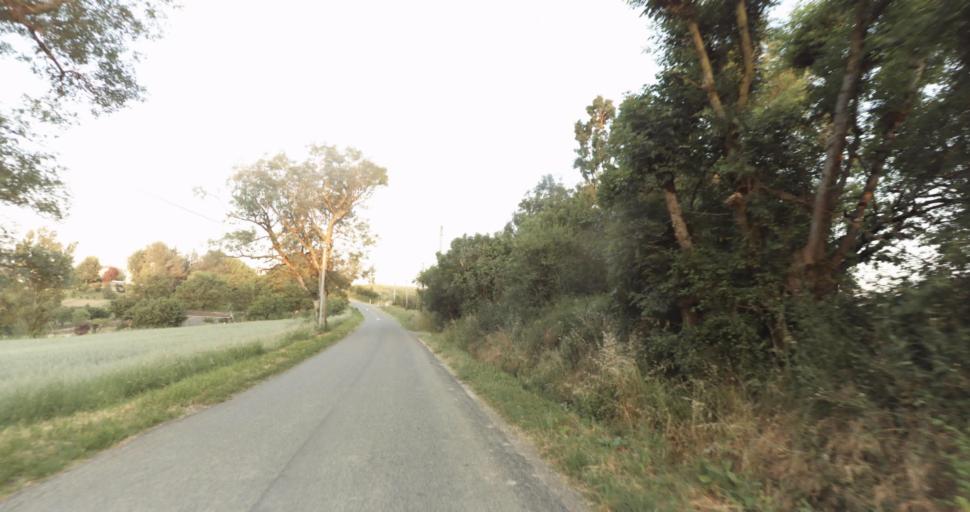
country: FR
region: Midi-Pyrenees
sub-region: Departement du Gers
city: Pujaudran
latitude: 43.6471
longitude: 1.1189
